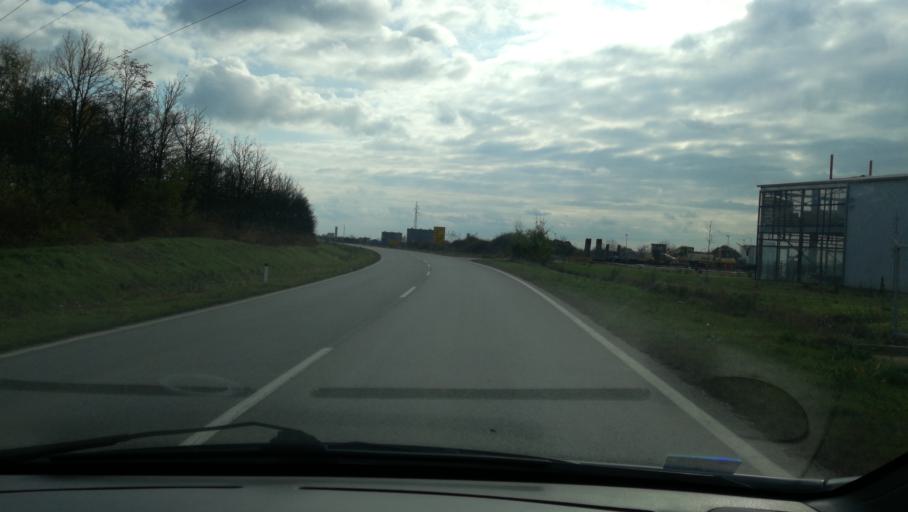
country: RS
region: Autonomna Pokrajina Vojvodina
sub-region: Severnobanatski Okrug
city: Kikinda
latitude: 45.8092
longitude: 20.4326
